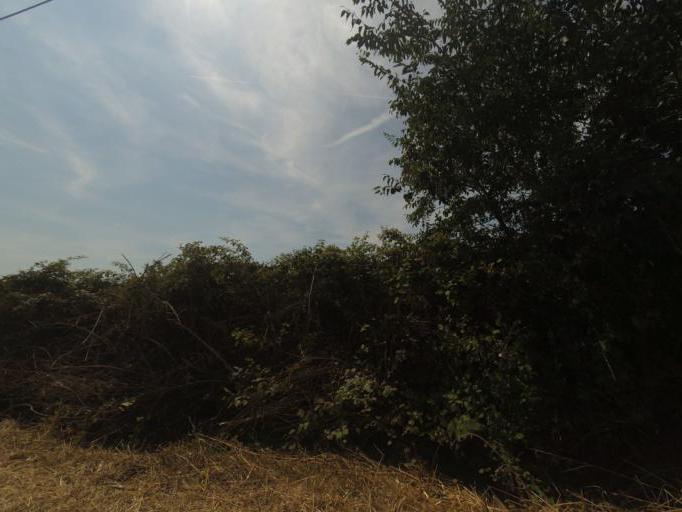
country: FR
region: Languedoc-Roussillon
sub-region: Departement du Gard
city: Aubais
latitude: 43.7694
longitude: 4.1280
